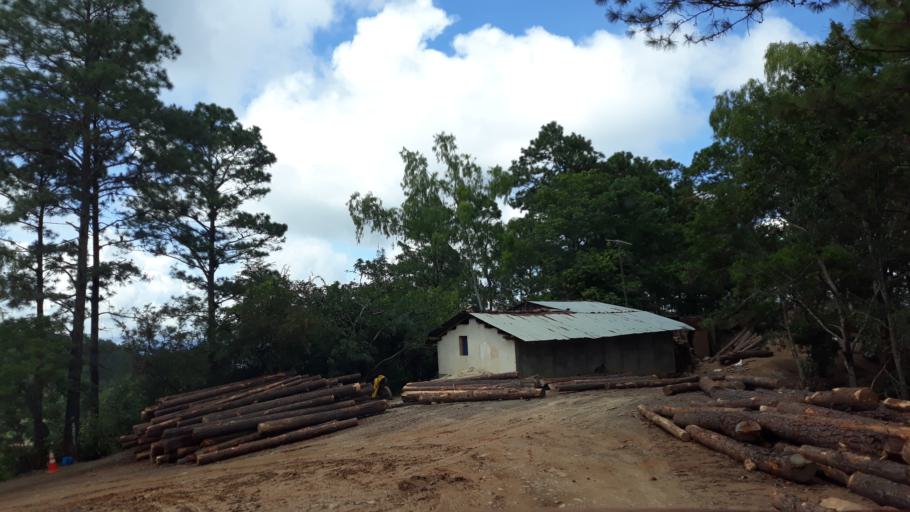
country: HN
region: El Paraiso
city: Santa Cruz
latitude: 13.7572
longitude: -86.6553
